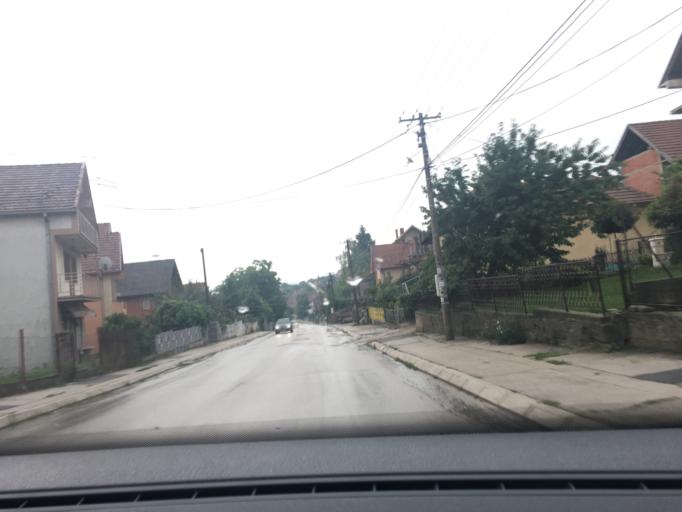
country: RS
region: Central Serbia
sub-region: Nisavski Okrug
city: Aleksinac
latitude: 43.5499
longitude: 21.7071
